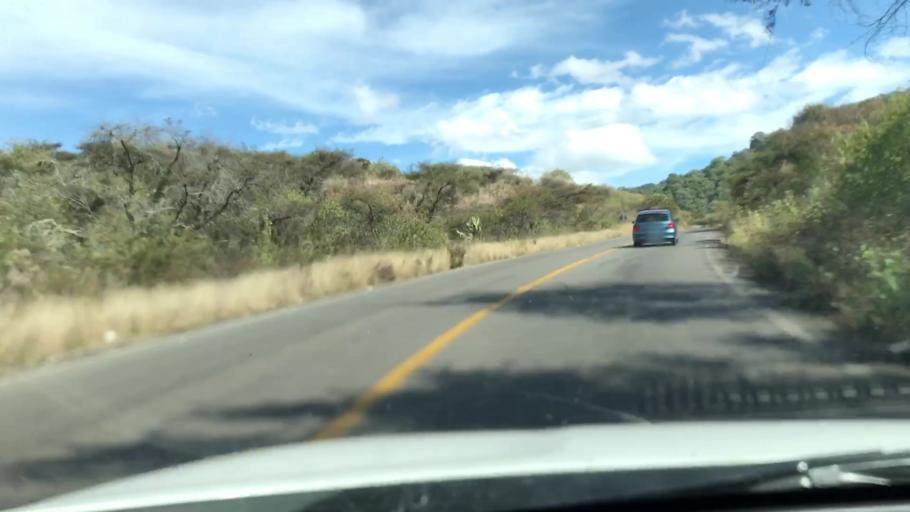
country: MX
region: Jalisco
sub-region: Zacoalco de Torres
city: Barranca de Otates (Barranca de Otatan)
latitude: 20.1925
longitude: -103.6996
